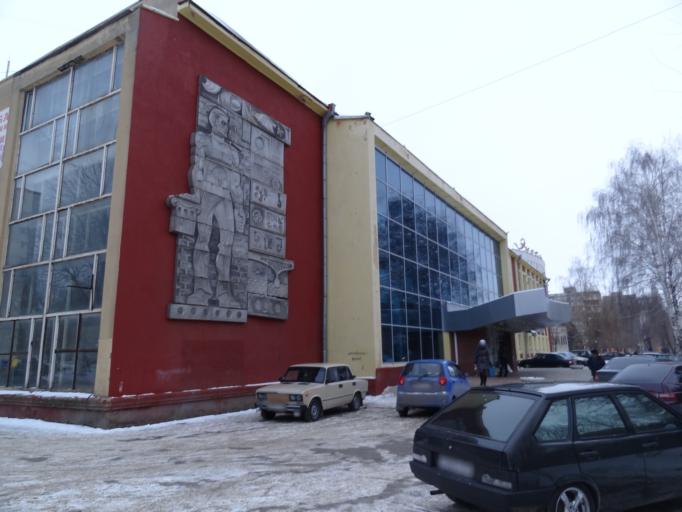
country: RU
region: Saratov
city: Engel's
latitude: 51.4774
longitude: 46.1306
